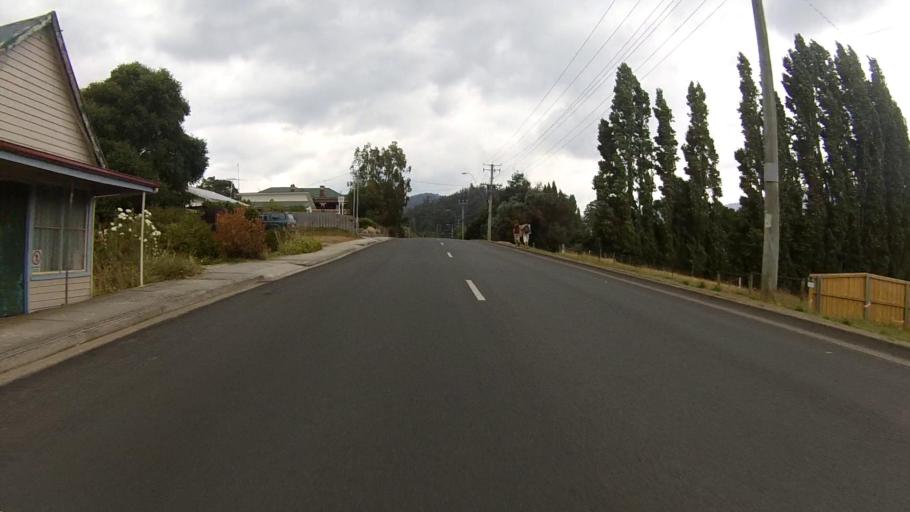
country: AU
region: Tasmania
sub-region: Huon Valley
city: Cygnet
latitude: -43.1577
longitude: 147.0746
